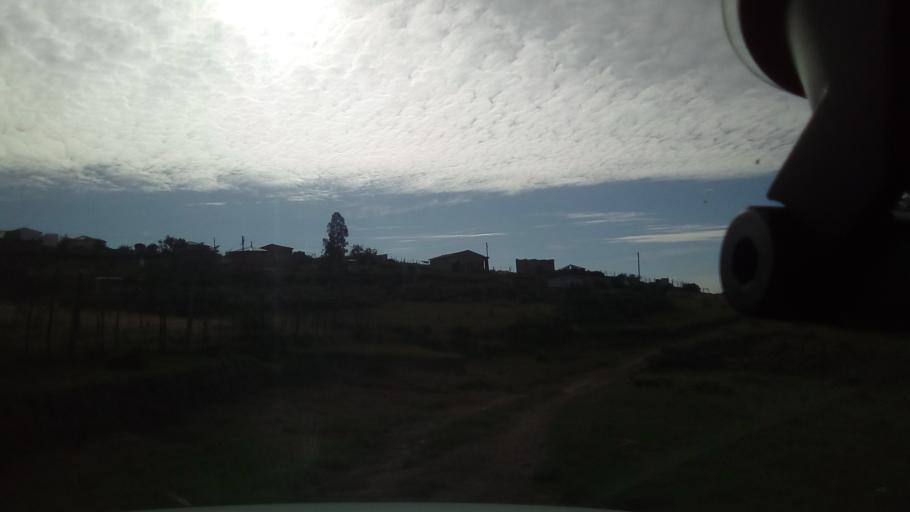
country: ZA
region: Eastern Cape
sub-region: Buffalo City Metropolitan Municipality
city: East London
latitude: -32.8015
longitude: 27.9631
